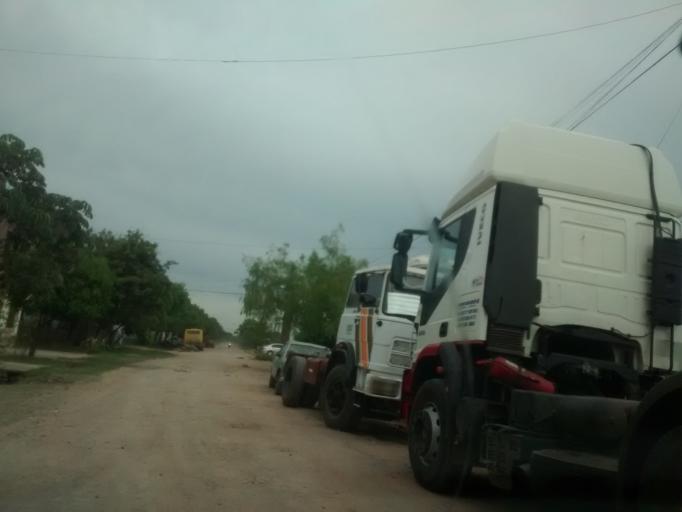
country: AR
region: Chaco
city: Resistencia
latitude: -27.4489
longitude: -59.0091
